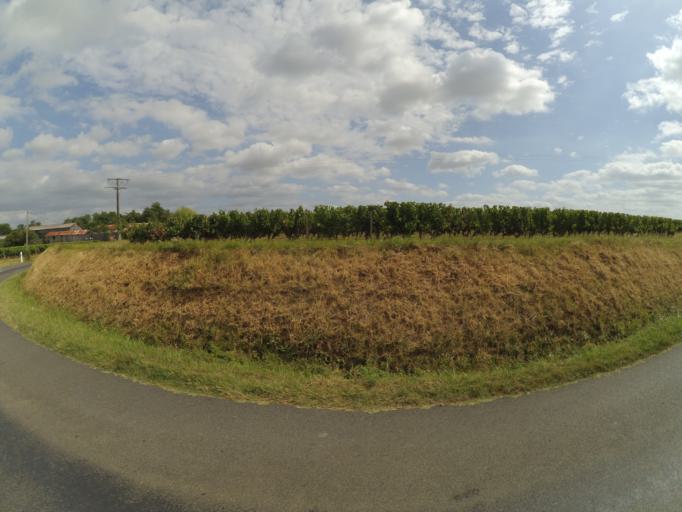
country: FR
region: Pays de la Loire
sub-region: Departement de Maine-et-Loire
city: Saint-Jean
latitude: 47.1934
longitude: -0.3685
